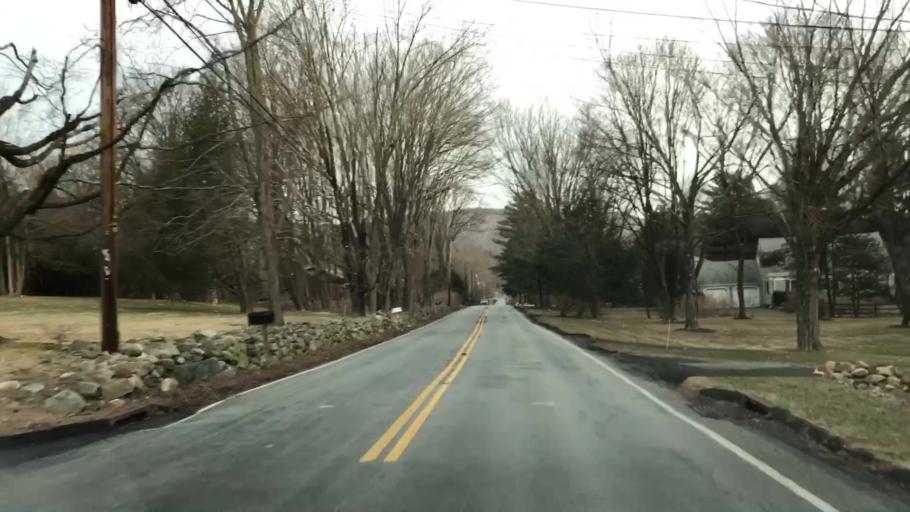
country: US
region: New York
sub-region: Rockland County
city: Viola
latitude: 41.1449
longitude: -74.0984
